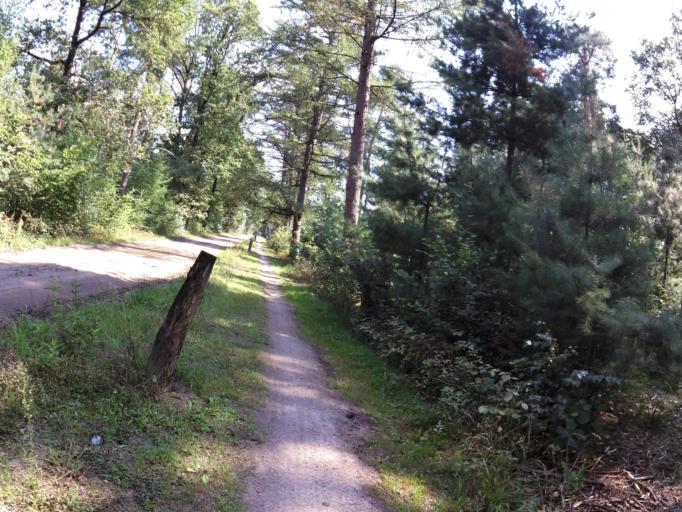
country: DE
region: North Rhine-Westphalia
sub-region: Regierungsbezirk Munster
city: Ahaus
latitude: 52.0233
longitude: 7.0007
